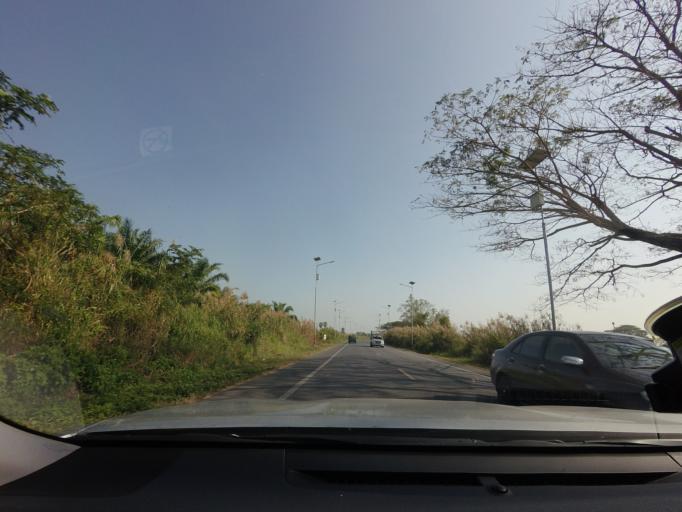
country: TH
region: Nakhon Si Thammarat
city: Nakhon Si Thammarat
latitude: 8.4644
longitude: 99.9798
